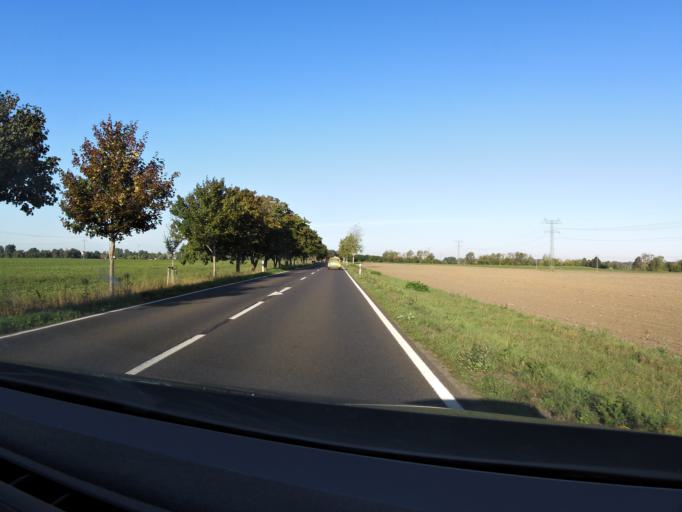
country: DE
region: Mecklenburg-Vorpommern
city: Anklam
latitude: 53.8528
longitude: 13.6524
